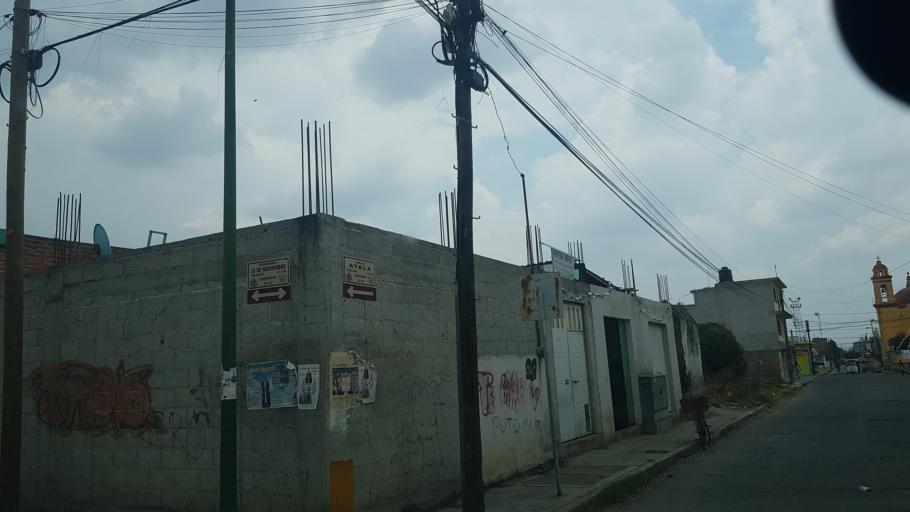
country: MX
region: Puebla
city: Huejotzingo
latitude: 19.1618
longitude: -98.4120
